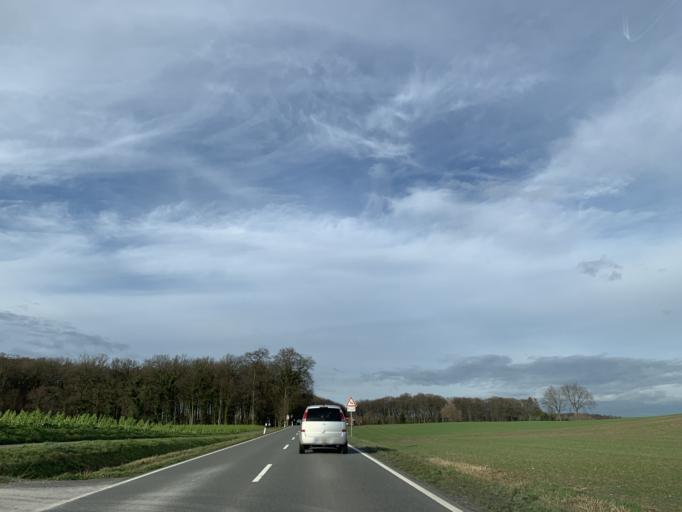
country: DE
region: North Rhine-Westphalia
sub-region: Regierungsbezirk Munster
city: Nottuln
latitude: 51.9381
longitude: 7.3365
